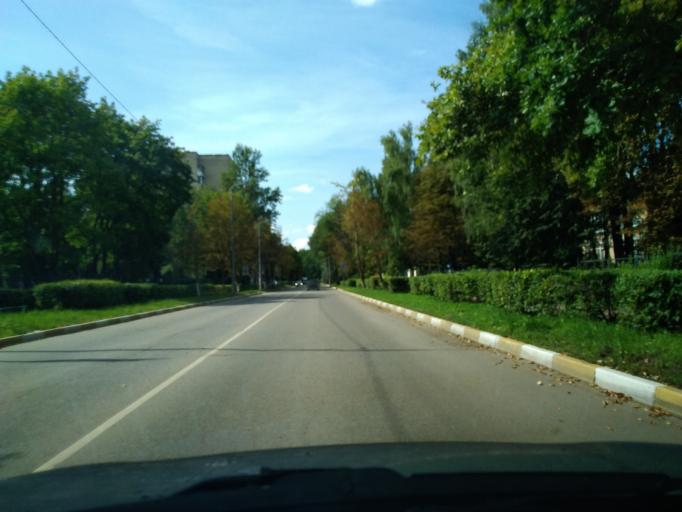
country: RU
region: Moskovskaya
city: Voskresensk
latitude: 55.3264
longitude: 38.6636
